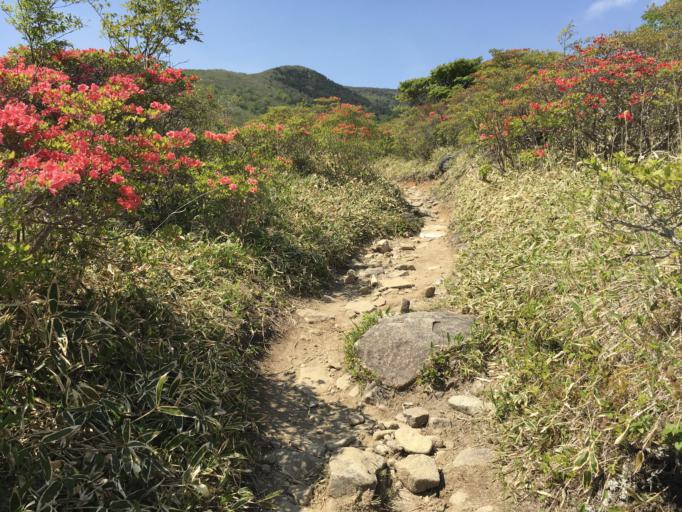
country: JP
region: Iwate
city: Ofunato
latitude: 39.1851
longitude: 141.7339
